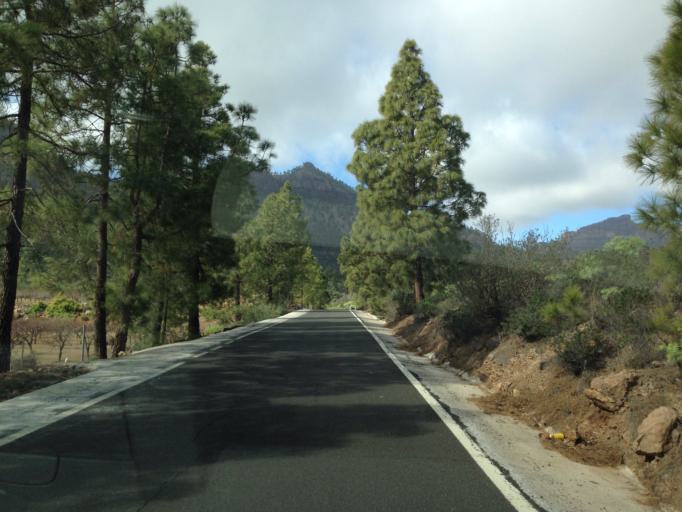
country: ES
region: Canary Islands
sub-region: Provincia de Las Palmas
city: San Bartolome
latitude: 27.9108
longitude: -15.5705
